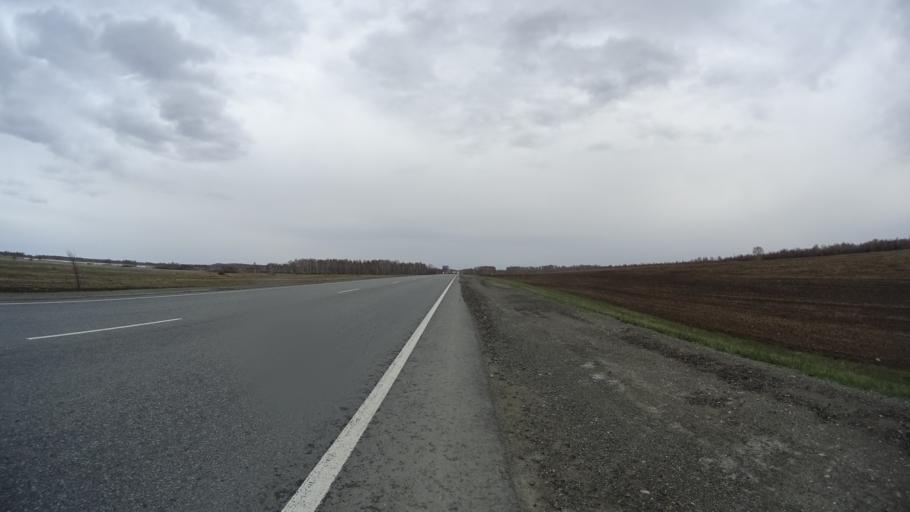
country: RU
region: Chelyabinsk
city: Krasnogorskiy
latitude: 54.6643
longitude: 61.2532
